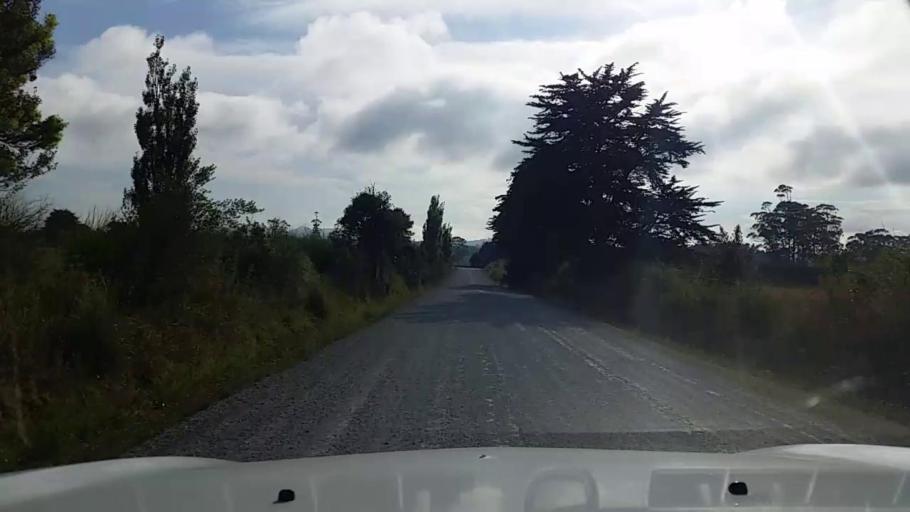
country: NZ
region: Northland
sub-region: Whangarei
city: Maungatapere
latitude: -35.6841
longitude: 174.1876
